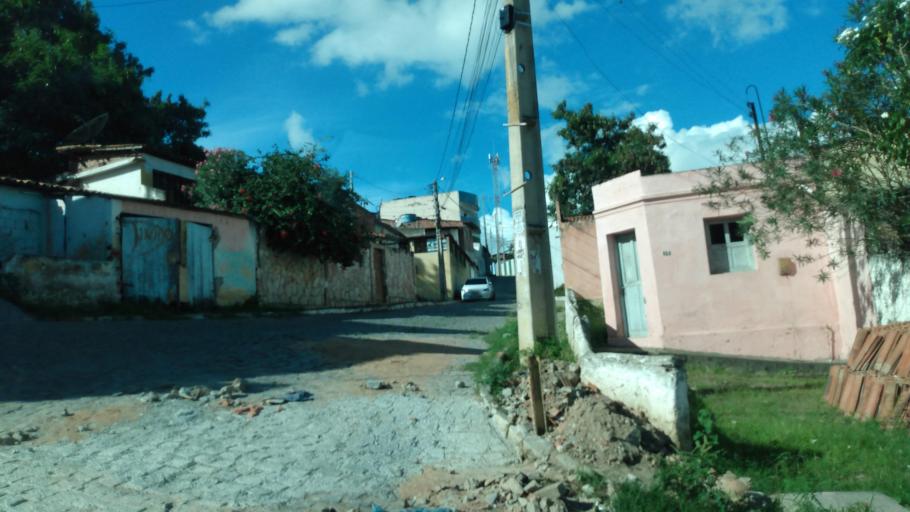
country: ET
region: Oromiya
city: Gore
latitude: 8.1996
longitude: 35.5679
